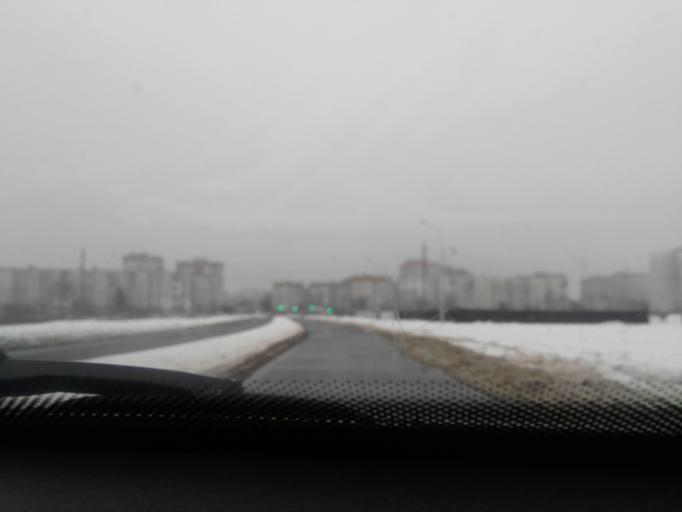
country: BY
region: Mogilev
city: Babruysk
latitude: 53.2010
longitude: 29.2234
